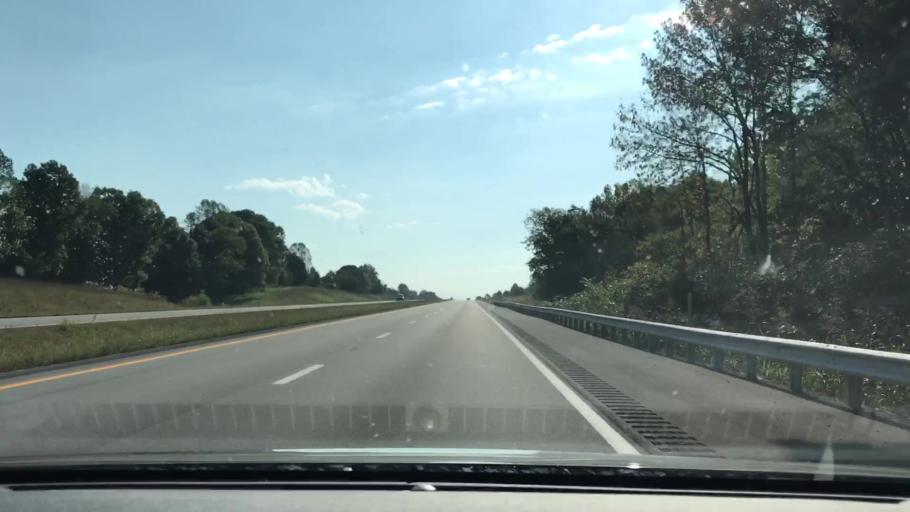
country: US
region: Kentucky
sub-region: Russell County
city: Russell Springs
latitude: 37.0521
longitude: -85.1597
